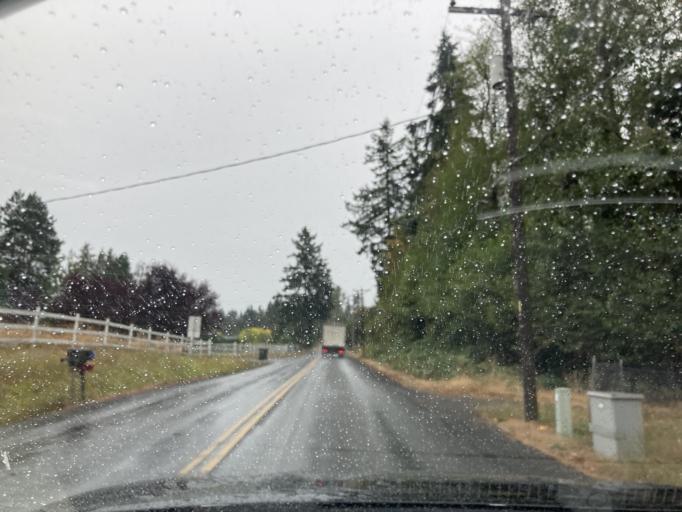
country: US
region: Washington
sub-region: Pierce County
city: Graham
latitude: 47.0414
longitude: -122.2876
